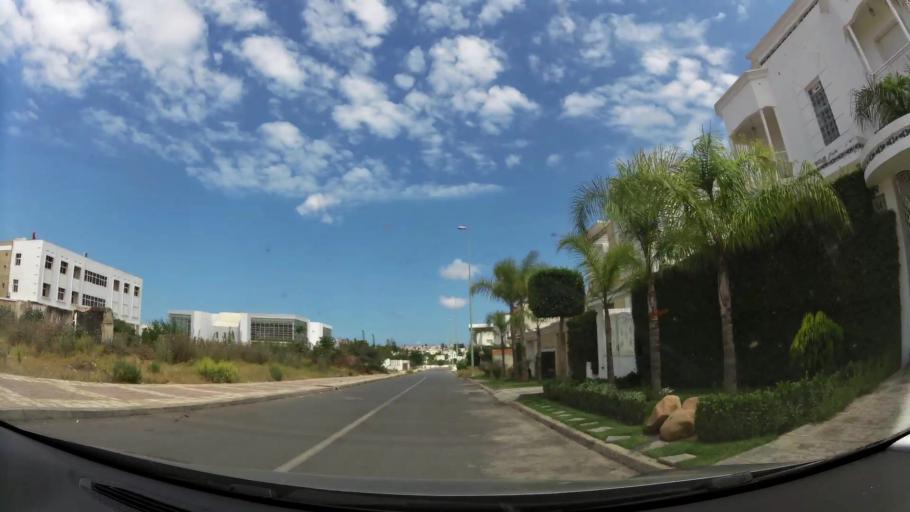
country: MA
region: Gharb-Chrarda-Beni Hssen
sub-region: Kenitra Province
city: Kenitra
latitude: 34.2524
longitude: -6.5982
